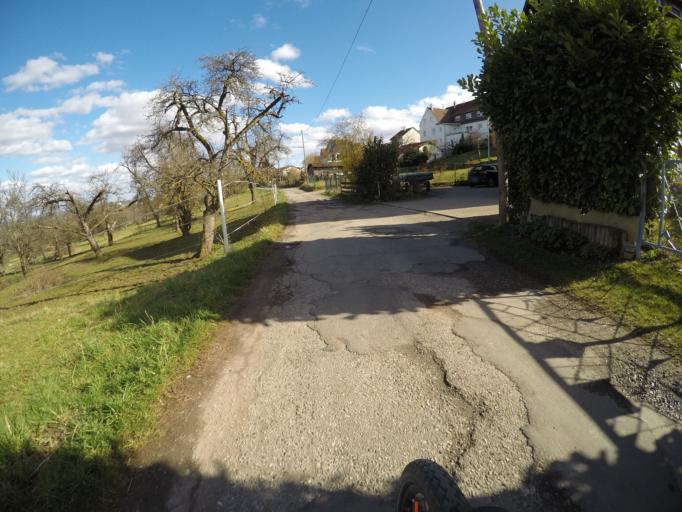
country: DE
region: Baden-Wuerttemberg
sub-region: Regierungsbezirk Stuttgart
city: Filderstadt
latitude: 48.6586
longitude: 9.1894
